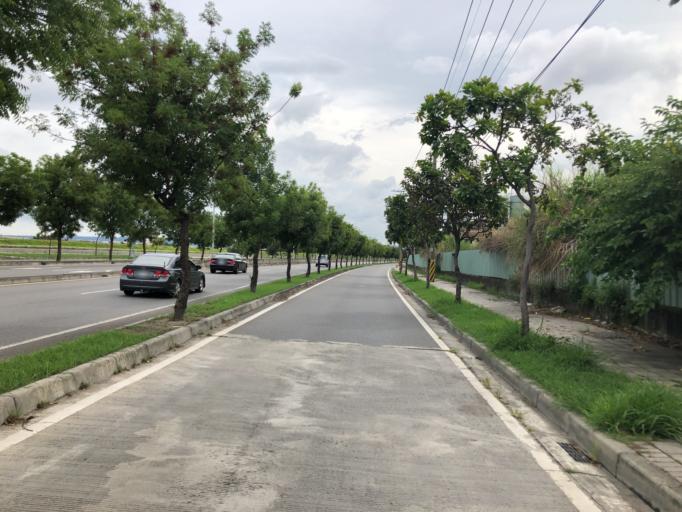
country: TW
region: Taiwan
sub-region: Taichung City
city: Taichung
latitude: 24.0856
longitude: 120.6761
